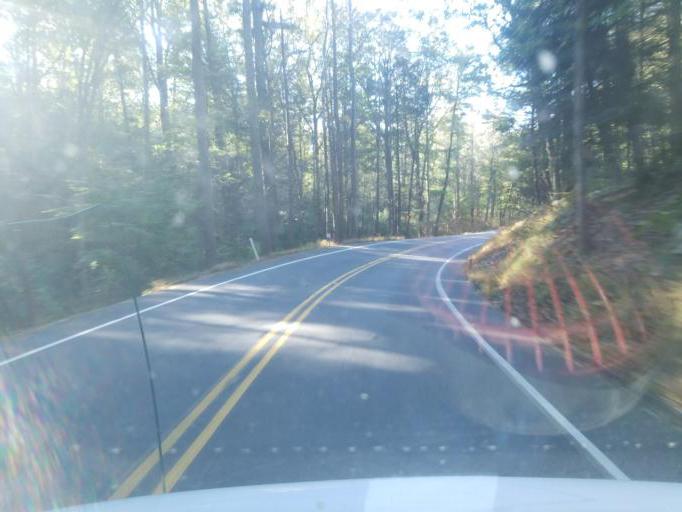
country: US
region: Pennsylvania
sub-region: Franklin County
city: Mont Alto
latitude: 39.8424
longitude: -77.5235
